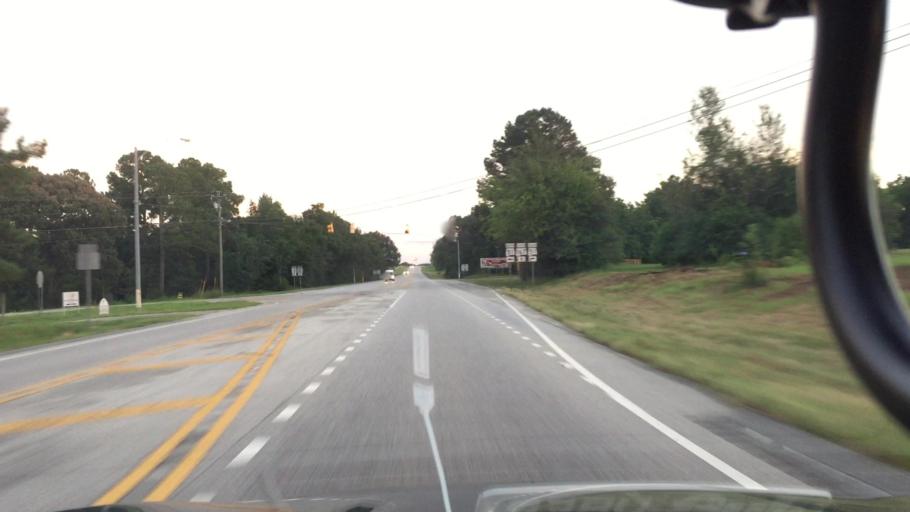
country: US
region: Alabama
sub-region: Coffee County
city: New Brockton
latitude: 31.4279
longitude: -85.8887
